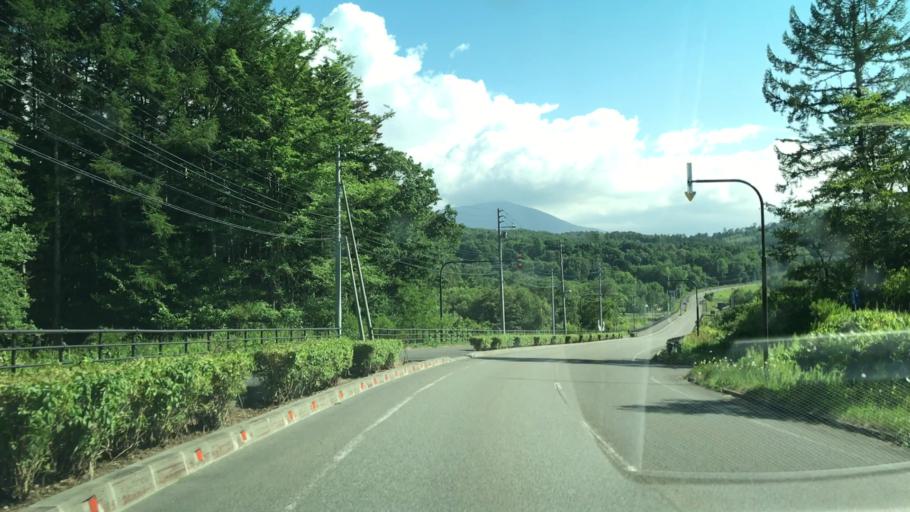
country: JP
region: Hokkaido
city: Shimo-furano
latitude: 42.8745
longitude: 142.4434
